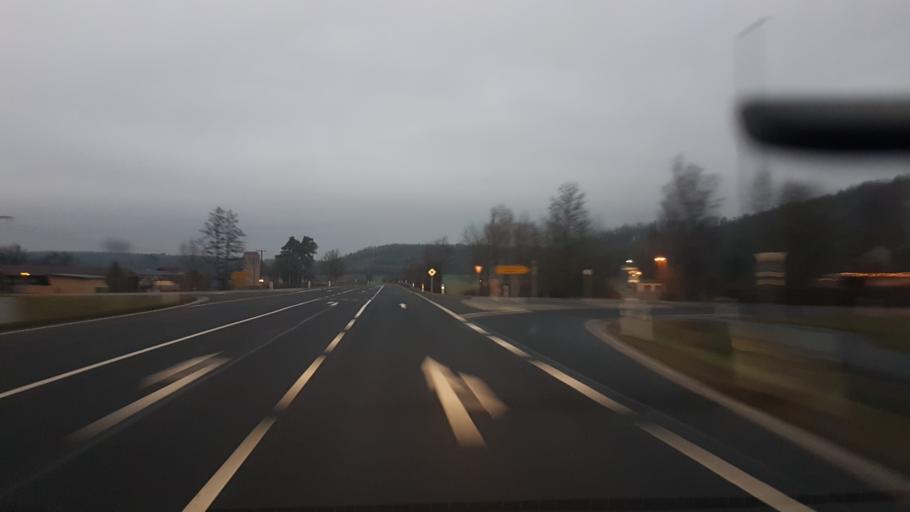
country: DE
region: Bavaria
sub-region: Regierungsbezirk Unterfranken
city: Ermershausen
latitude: 50.2388
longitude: 10.5689
